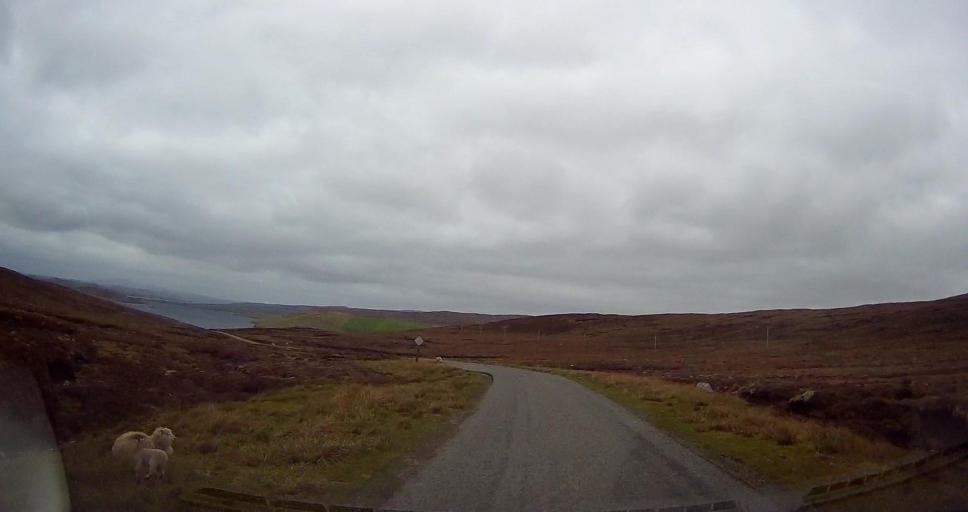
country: GB
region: Scotland
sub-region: Shetland Islands
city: Lerwick
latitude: 60.3202
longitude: -1.3382
